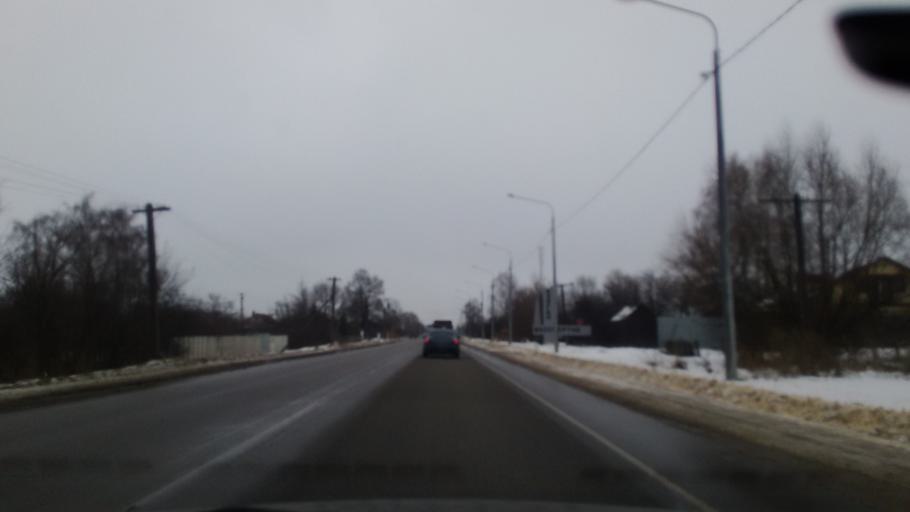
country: RU
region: Tula
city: Borodinskiy
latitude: 54.0226
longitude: 37.8978
